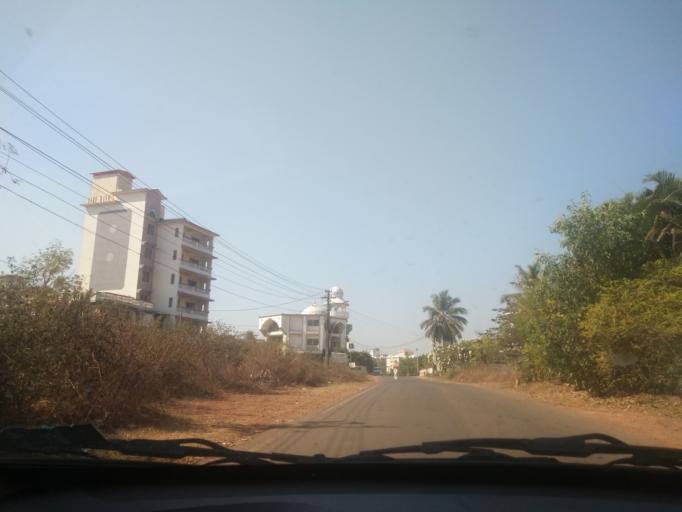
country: IN
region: Goa
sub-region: South Goa
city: Chicalim
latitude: 15.3919
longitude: 73.8609
